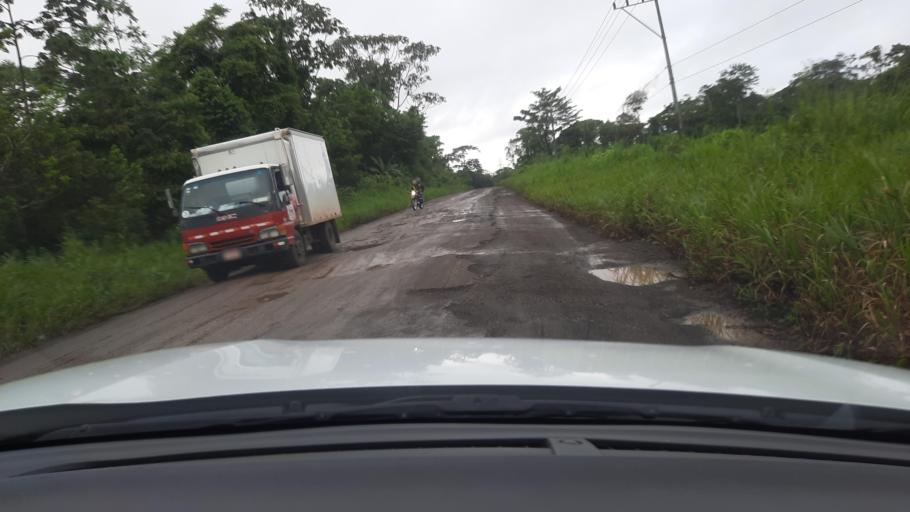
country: CR
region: Alajuela
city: San Jose
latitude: 11.0055
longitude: -85.3199
